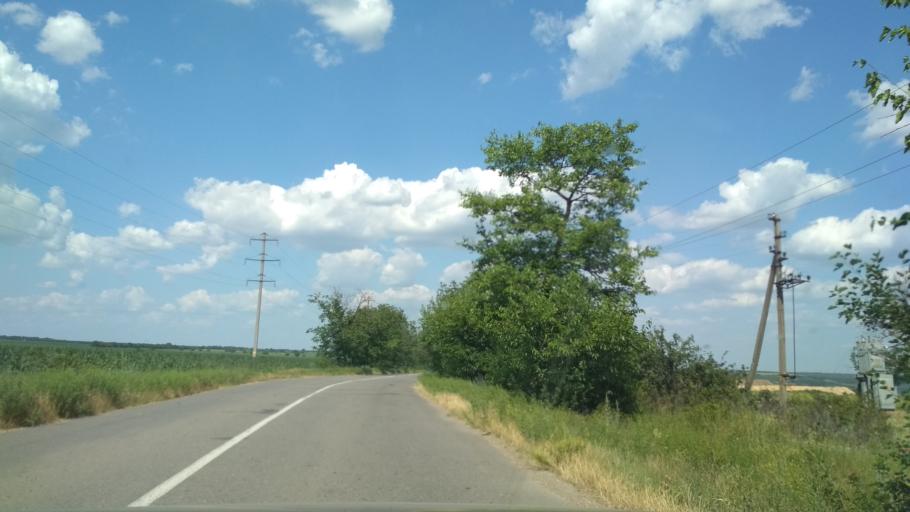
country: MD
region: Criuleni
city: Criuleni
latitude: 47.1627
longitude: 29.1707
